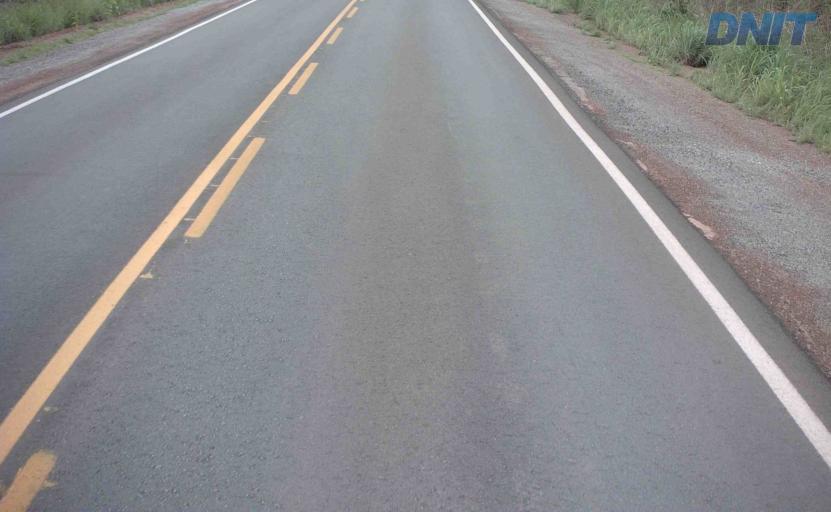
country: BR
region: Goias
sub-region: Padre Bernardo
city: Padre Bernardo
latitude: -15.4047
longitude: -48.2001
